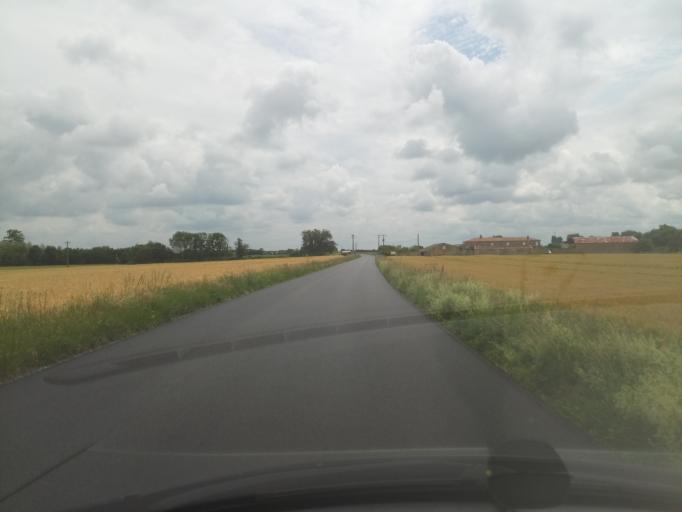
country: FR
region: Poitou-Charentes
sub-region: Departement de la Charente-Maritime
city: Saint-Jean-de-Liversay
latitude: 46.2715
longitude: -0.8970
